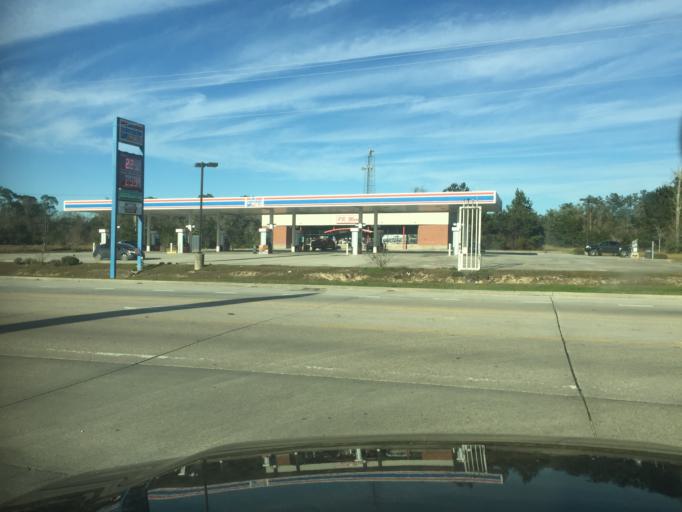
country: US
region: Louisiana
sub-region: Saint Tammany Parish
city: Pearl River
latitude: 30.3549
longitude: -89.7436
